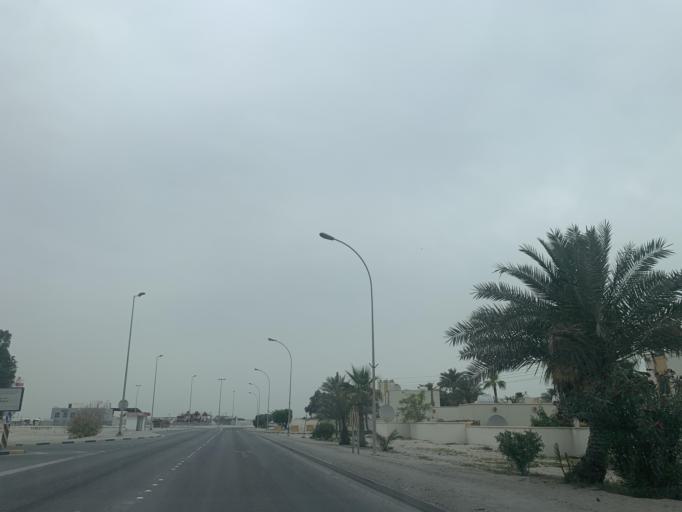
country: BH
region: Muharraq
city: Al Hadd
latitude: 26.2112
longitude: 50.6605
